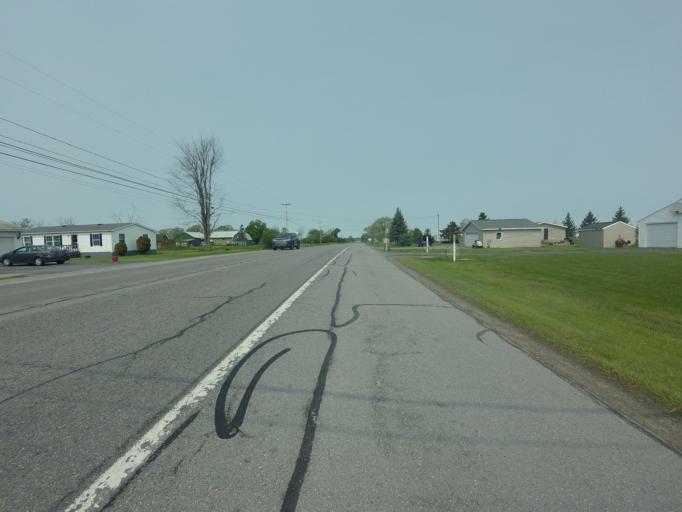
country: US
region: New York
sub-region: Jefferson County
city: Dexter
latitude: 44.0418
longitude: -76.0806
